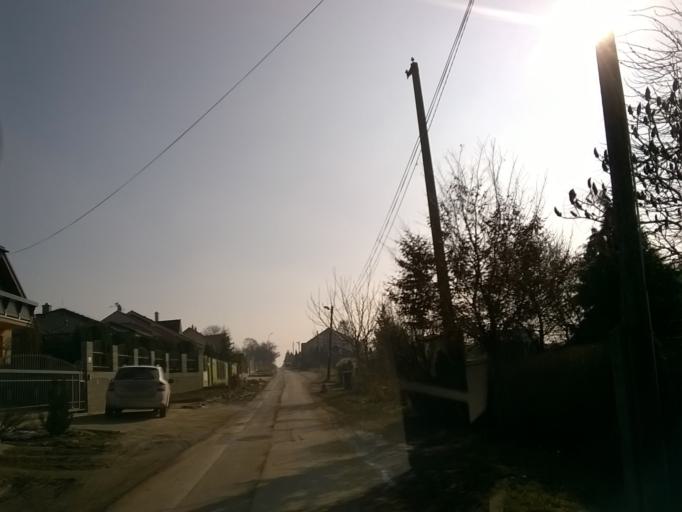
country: SK
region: Nitriansky
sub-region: Okres Nitra
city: Nitra
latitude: 48.3007
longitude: 18.0481
